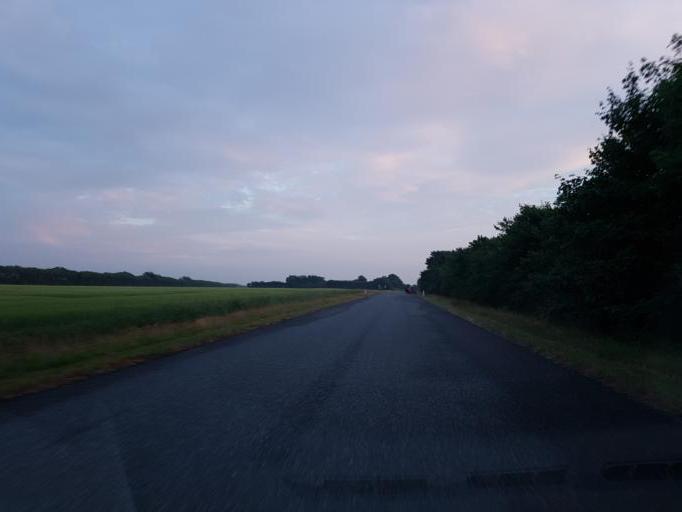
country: DK
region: South Denmark
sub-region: Esbjerg Kommune
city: Tjaereborg
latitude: 55.5164
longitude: 8.5689
